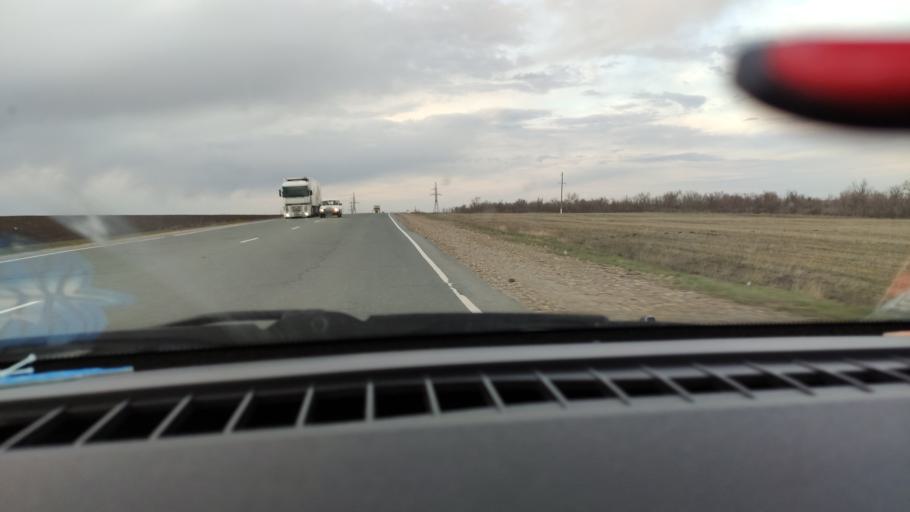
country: RU
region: Saratov
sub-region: Saratovskiy Rayon
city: Saratov
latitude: 51.7470
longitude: 46.0546
